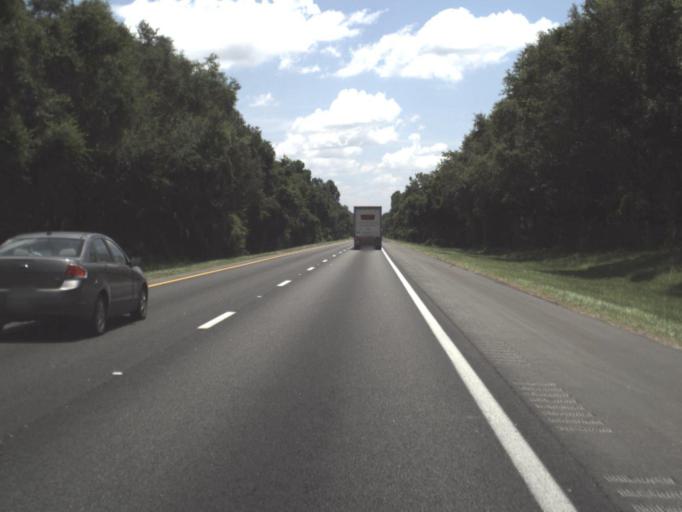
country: US
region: Florida
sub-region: Madison County
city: Madison
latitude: 30.4102
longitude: -83.4196
